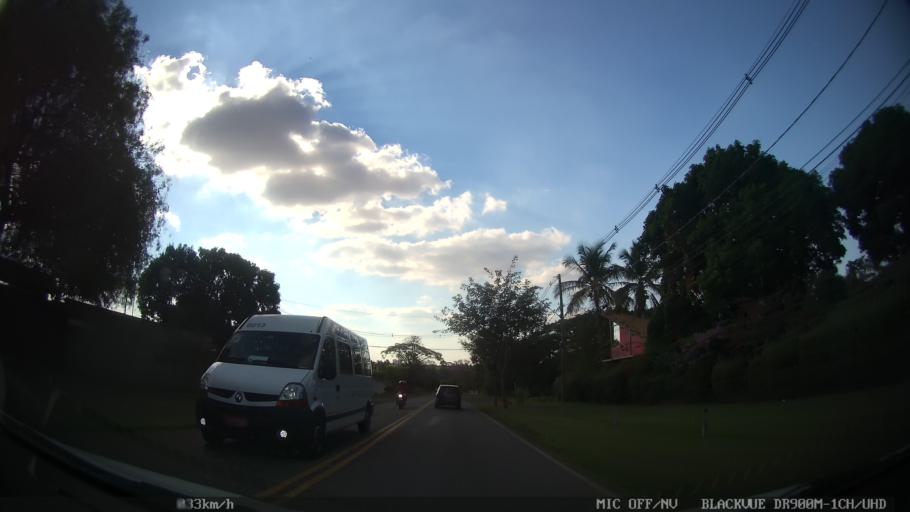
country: BR
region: Sao Paulo
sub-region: Nova Odessa
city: Nova Odessa
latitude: -22.7996
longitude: -47.3354
